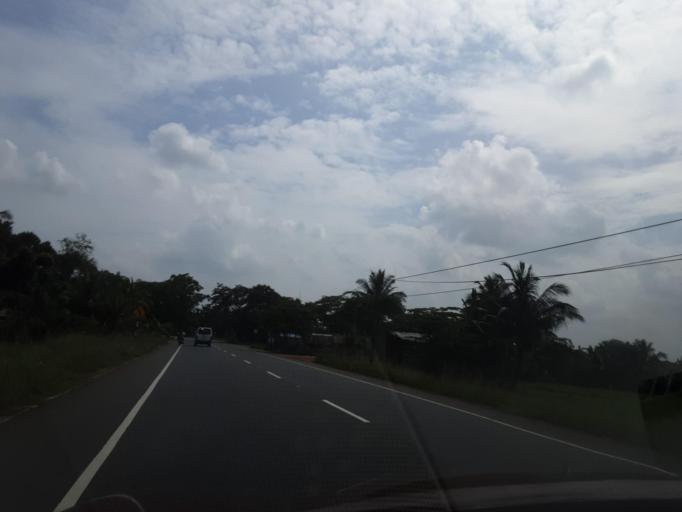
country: LK
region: North Central
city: Anuradhapura
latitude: 8.5063
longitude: 80.5079
